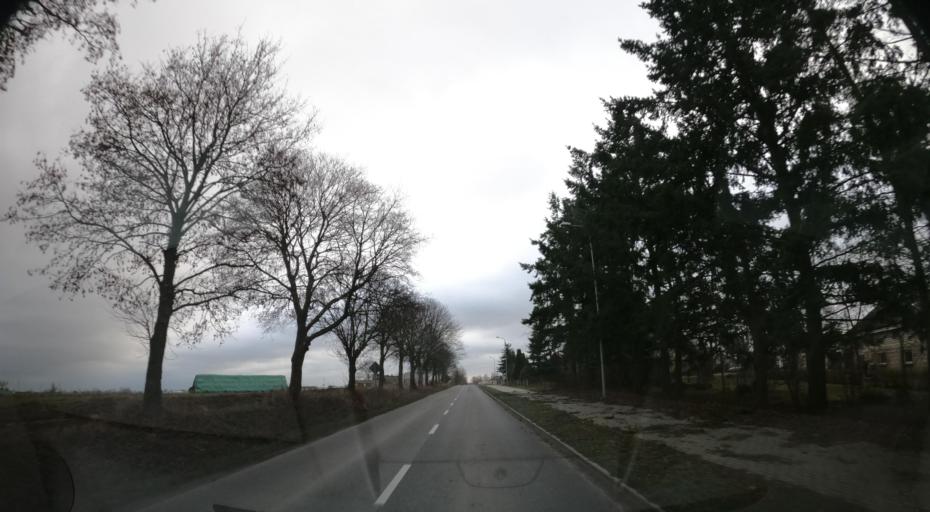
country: PL
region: Kujawsko-Pomorskie
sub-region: Powiat nakielski
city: Sadki
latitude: 53.1656
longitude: 17.4408
